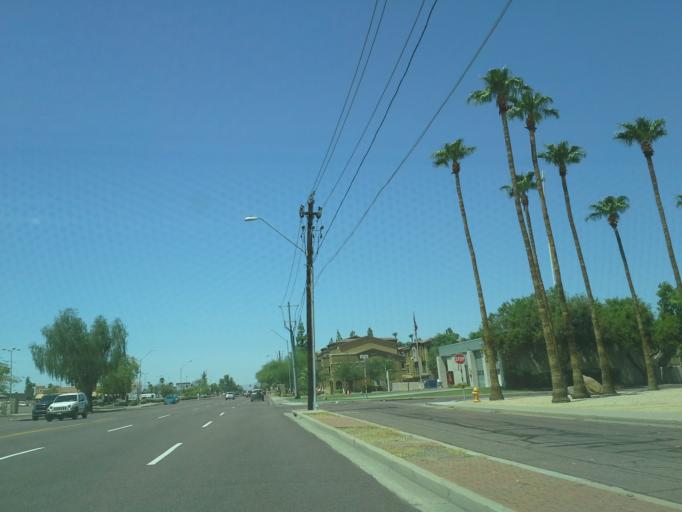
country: US
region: Arizona
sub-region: Maricopa County
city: Glendale
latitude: 33.6254
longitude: -112.1282
